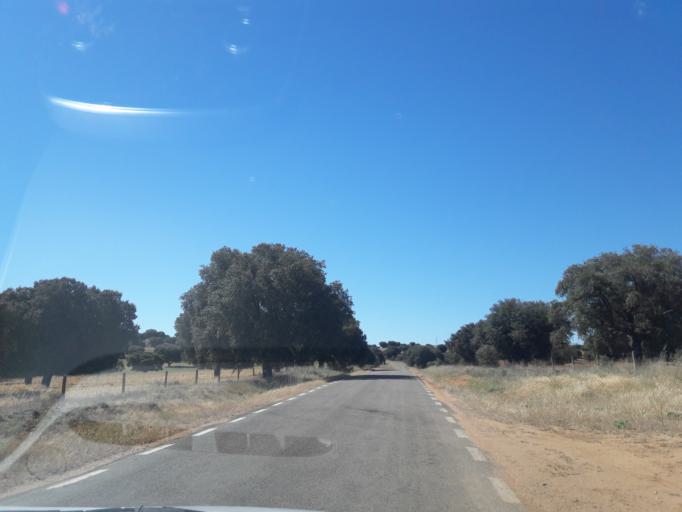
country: ES
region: Castille and Leon
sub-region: Provincia de Salamanca
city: Parada de Arriba
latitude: 41.0090
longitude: -5.8141
